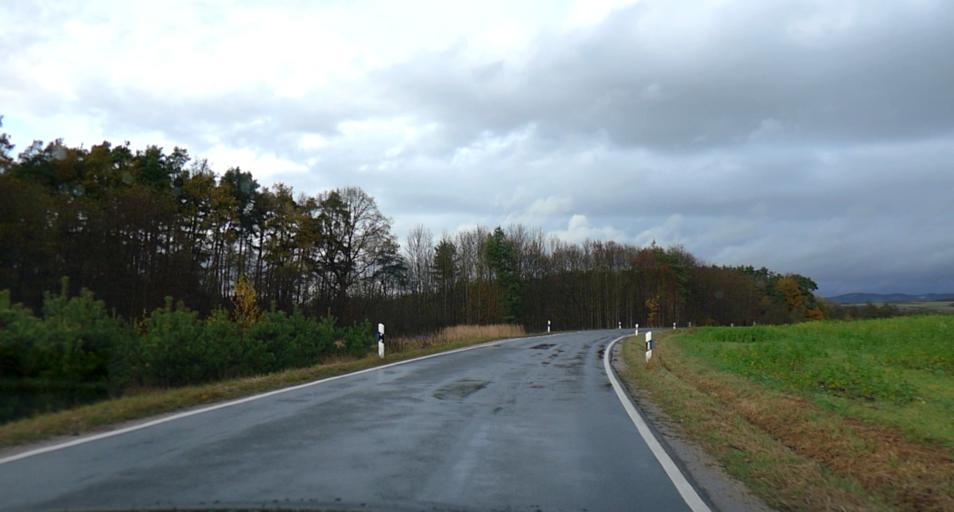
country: DE
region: Bavaria
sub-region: Upper Franconia
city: Langensendelbach
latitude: 49.6497
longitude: 11.0813
